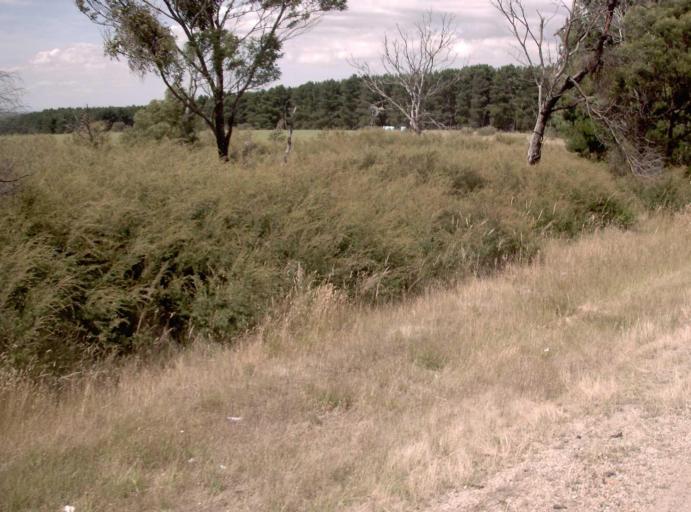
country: AU
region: Victoria
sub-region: Wellington
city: Sale
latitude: -38.1713
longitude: 146.9759
